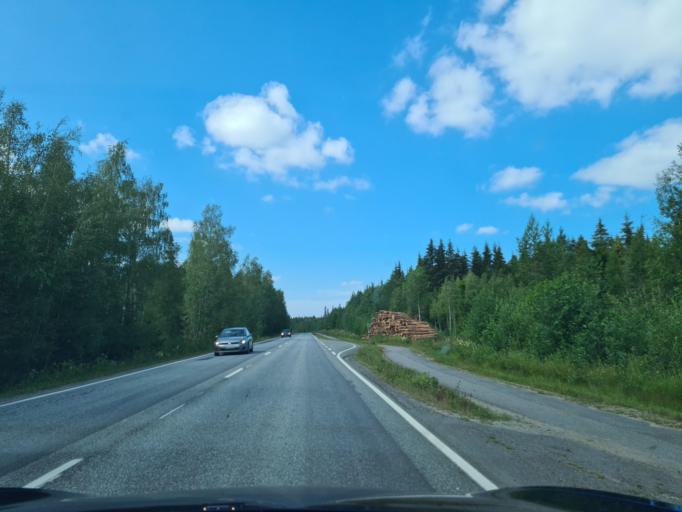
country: FI
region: Ostrobothnia
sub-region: Vaasa
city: Replot
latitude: 63.2010
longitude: 21.5322
